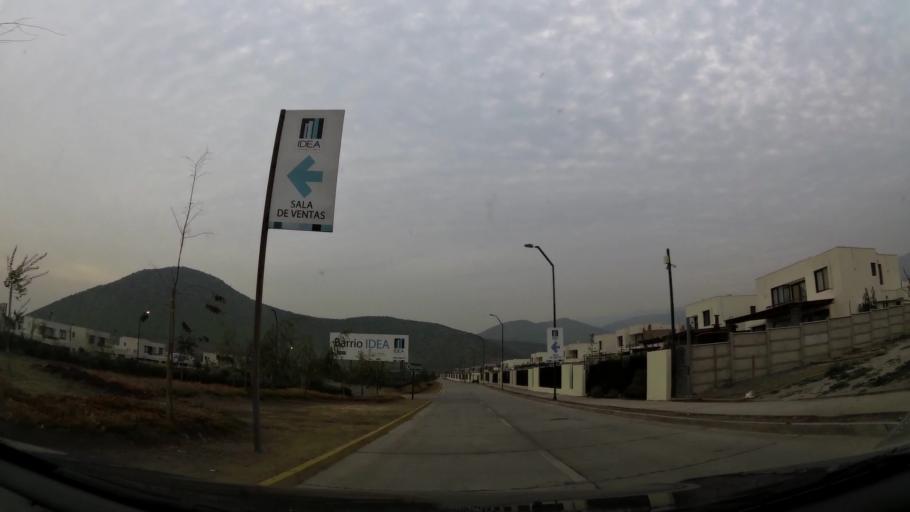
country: CL
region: Santiago Metropolitan
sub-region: Provincia de Chacabuco
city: Chicureo Abajo
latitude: -33.3202
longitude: -70.6458
